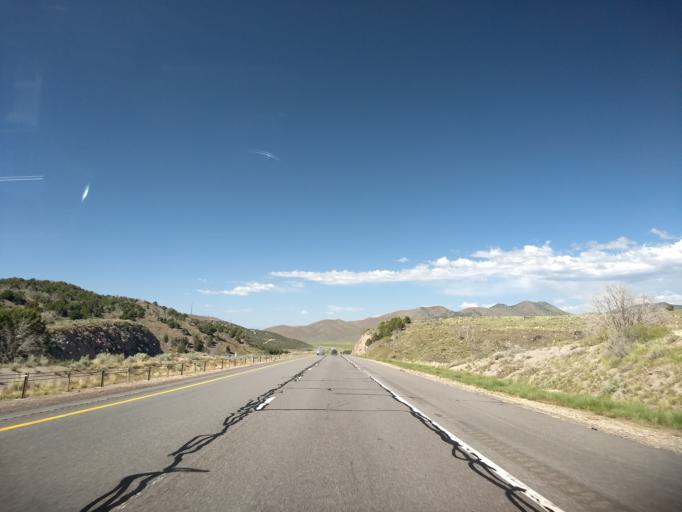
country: US
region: Utah
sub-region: Beaver County
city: Beaver
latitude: 38.6412
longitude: -112.6064
